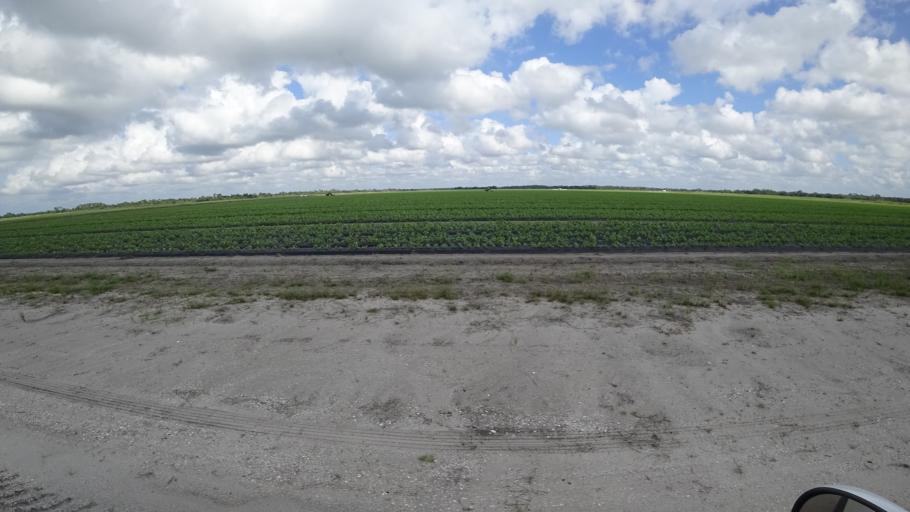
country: US
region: Florida
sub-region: Sarasota County
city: Lake Sarasota
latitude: 27.4034
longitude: -82.2065
